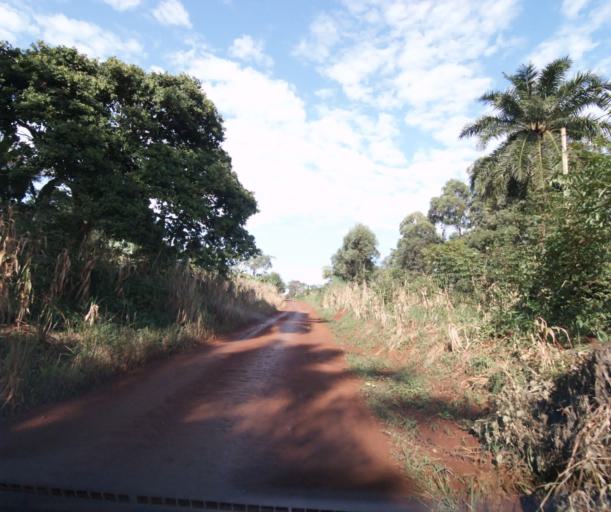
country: CM
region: West
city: Mbouda
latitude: 5.6222
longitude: 10.3231
